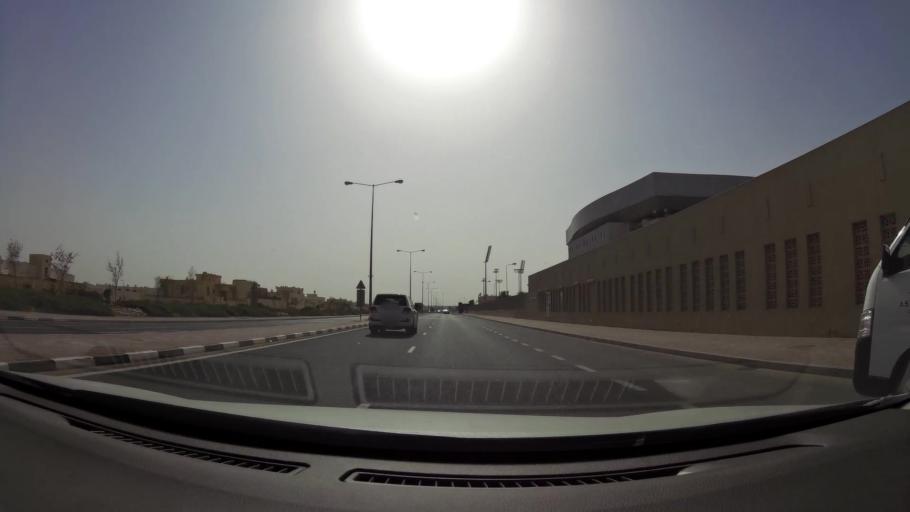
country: QA
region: Baladiyat ar Rayyan
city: Ar Rayyan
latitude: 25.3450
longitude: 51.4455
